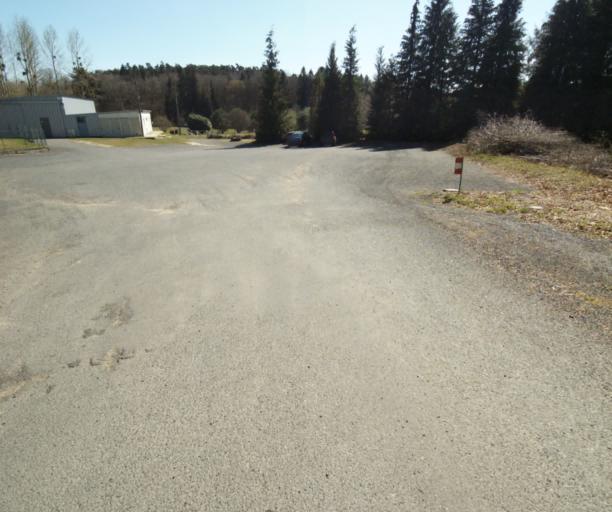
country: FR
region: Limousin
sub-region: Departement de la Correze
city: Chameyrat
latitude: 45.2684
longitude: 1.6928
